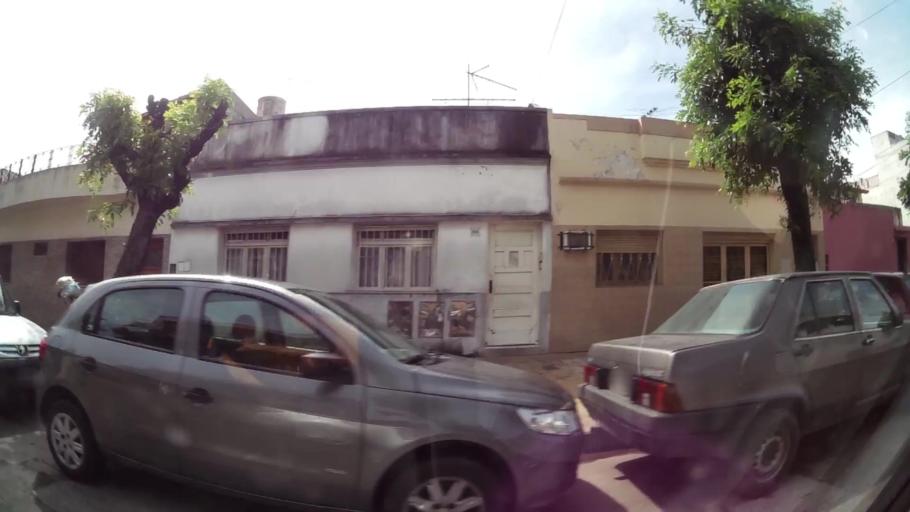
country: AR
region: Buenos Aires F.D.
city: Villa Lugano
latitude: -34.6558
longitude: -58.4356
